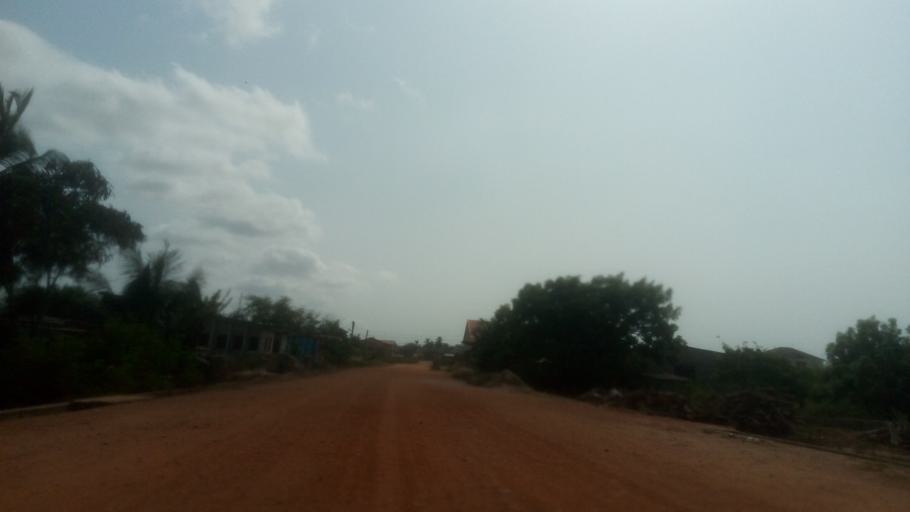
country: GH
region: Central
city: Winneba
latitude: 5.3544
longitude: -0.6353
